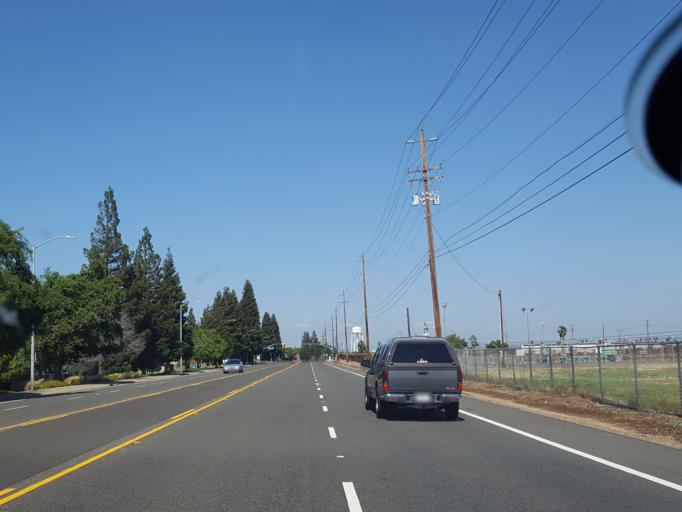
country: US
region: California
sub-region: Sacramento County
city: Rancho Cordova
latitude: 38.5632
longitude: -121.3141
